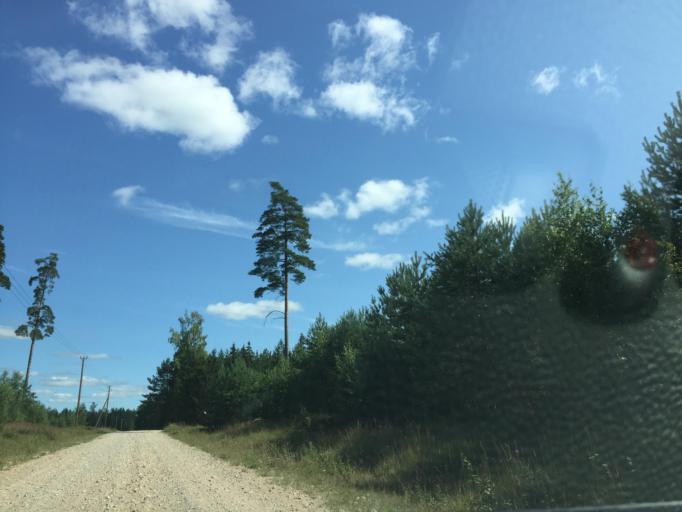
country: LV
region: Talsu Rajons
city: Stende
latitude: 57.1765
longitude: 22.3099
